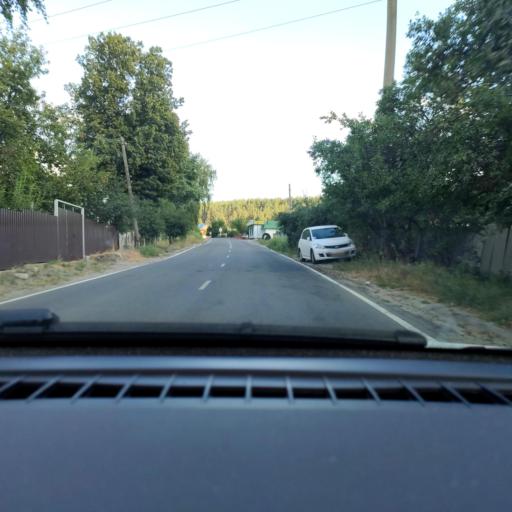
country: RU
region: Voronezj
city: Devitsa
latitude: 51.6556
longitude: 38.9782
